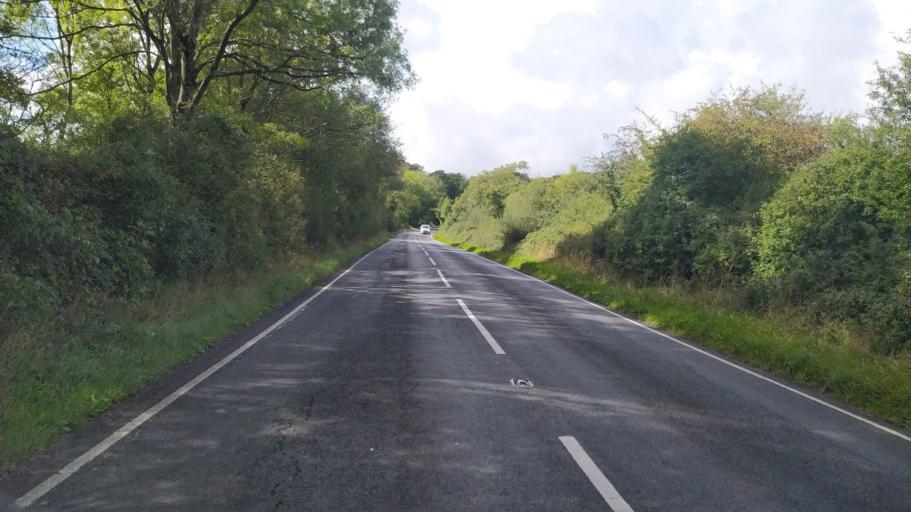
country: GB
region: England
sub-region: Dorset
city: Stalbridge
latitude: 50.9187
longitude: -2.3802
